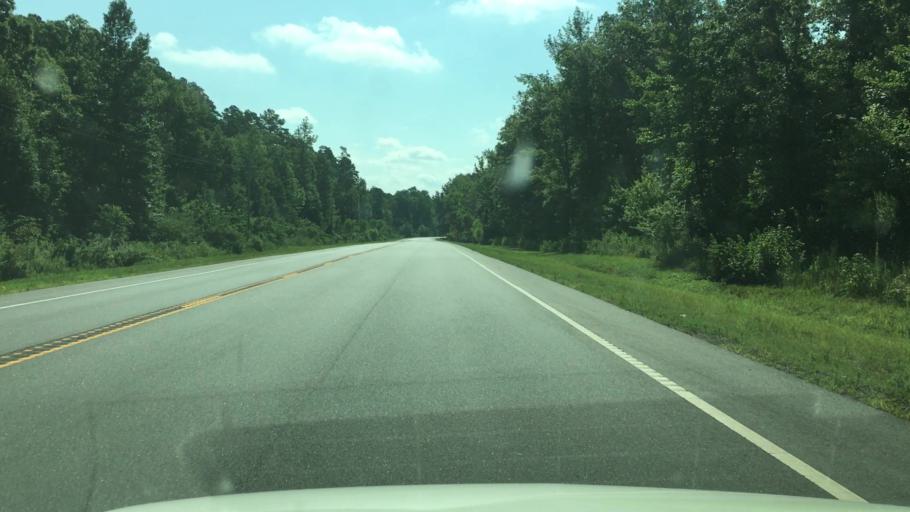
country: US
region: Arkansas
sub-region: Garland County
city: Rockwell
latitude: 34.5177
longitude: -93.3066
